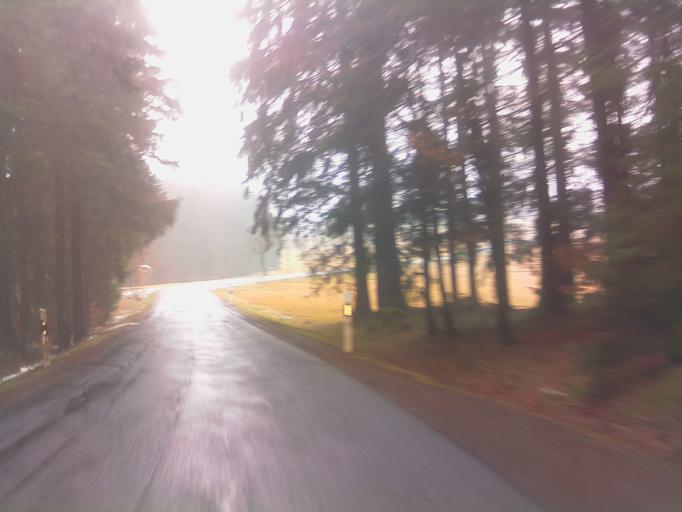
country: DE
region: Thuringia
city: Masserberg
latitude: 50.5170
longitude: 10.9342
